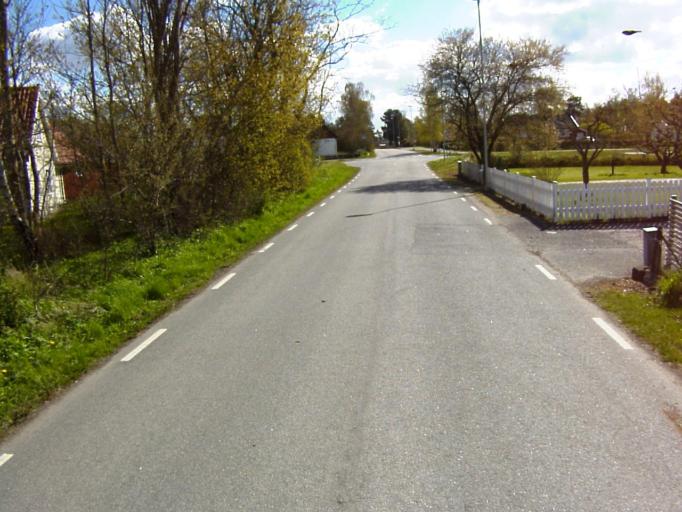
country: SE
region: Skane
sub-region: Kristianstads Kommun
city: Kristianstad
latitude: 56.0108
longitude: 14.0904
